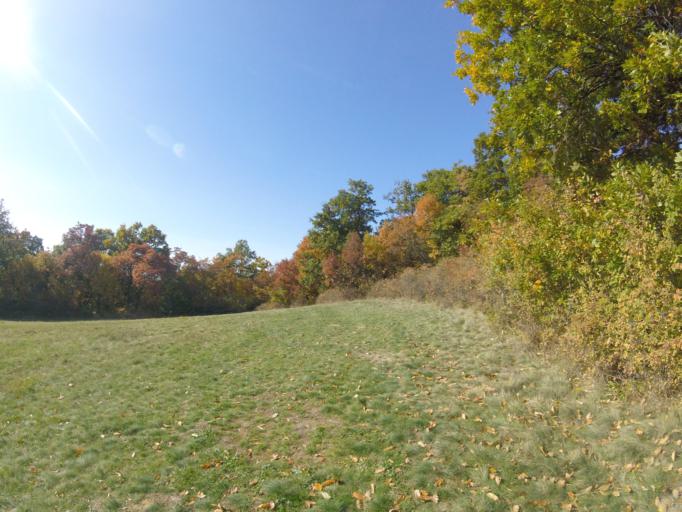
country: HU
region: Pest
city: Csobanka
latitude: 47.6439
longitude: 18.9481
